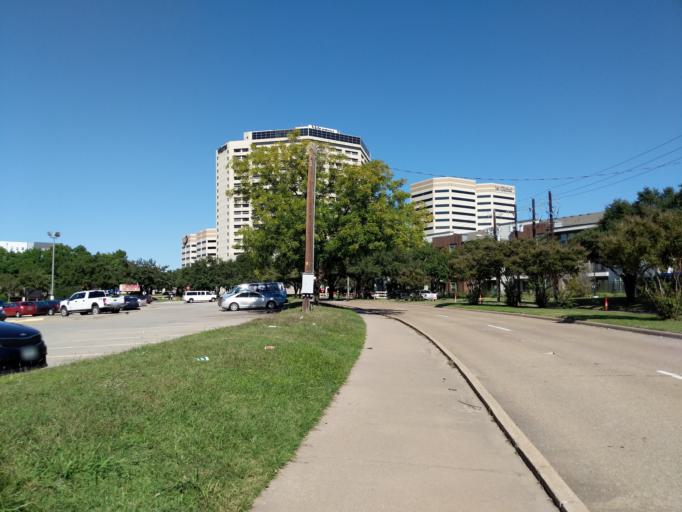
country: US
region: Texas
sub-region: Dallas County
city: Richardson
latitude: 32.9201
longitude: -96.7728
